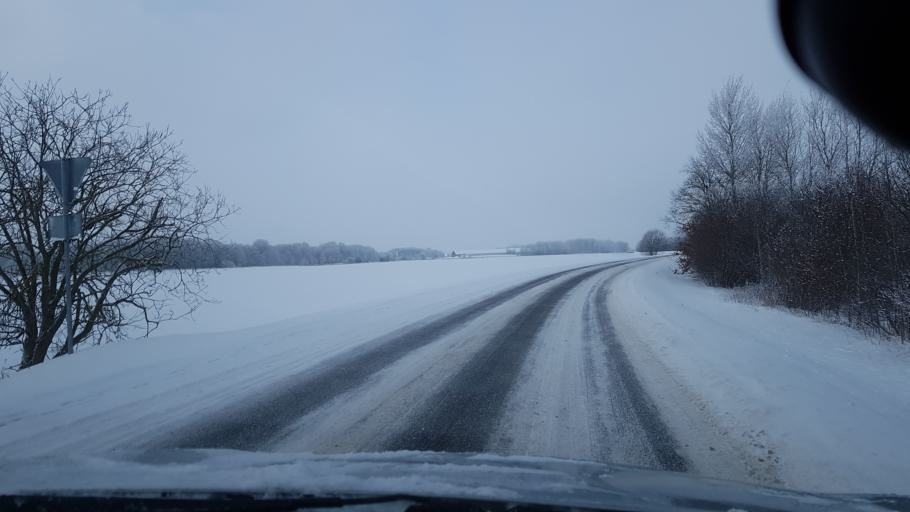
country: EE
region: Harju
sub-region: Keila linn
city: Keila
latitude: 59.3302
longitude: 24.4677
